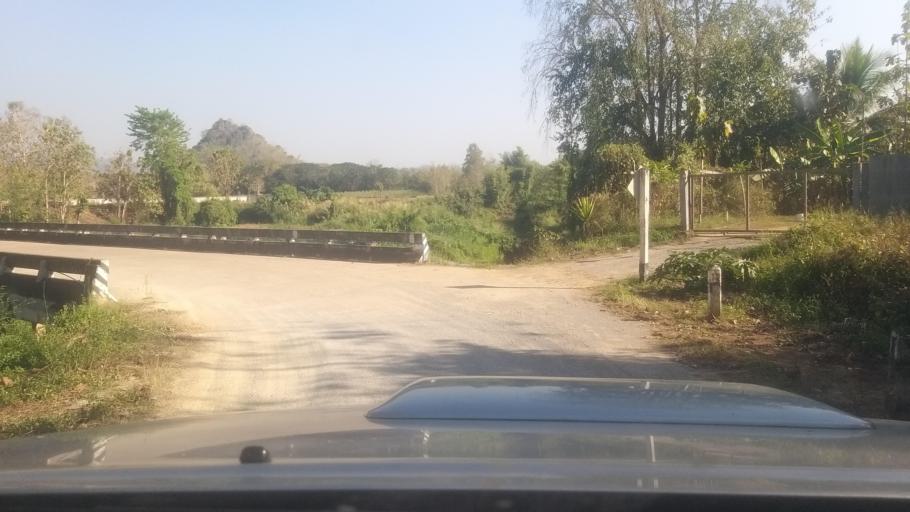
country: TH
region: Phrae
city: Phrae
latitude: 18.2642
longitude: 99.9859
